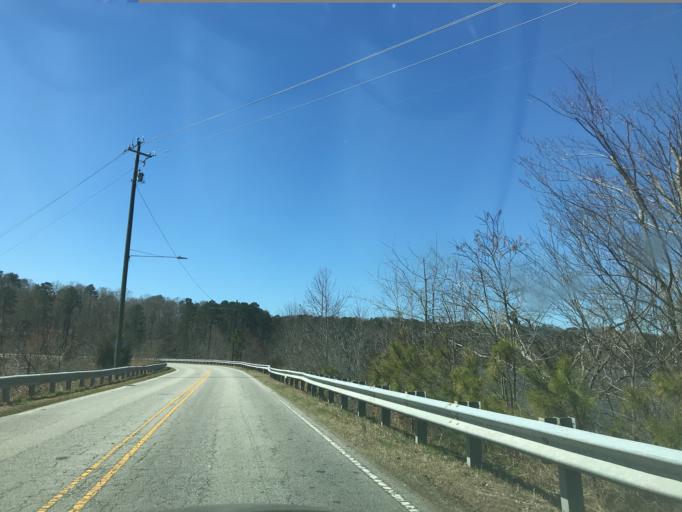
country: US
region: North Carolina
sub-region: Wake County
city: West Raleigh
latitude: 35.7625
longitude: -78.7154
